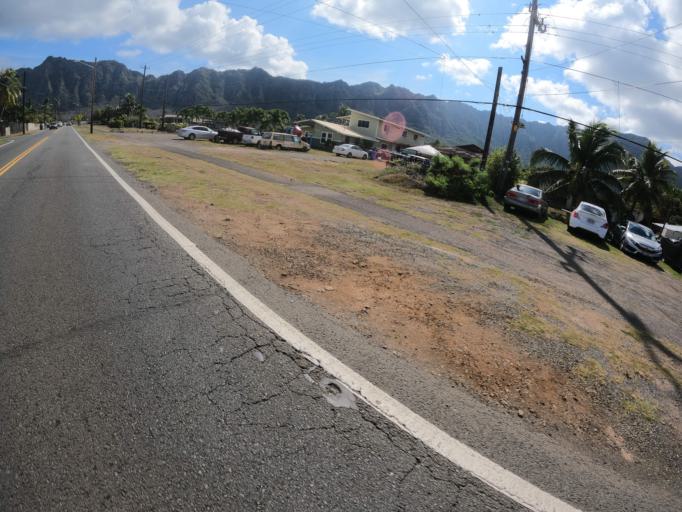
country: US
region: Hawaii
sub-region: Honolulu County
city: Waimanalo Beach
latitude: 21.3370
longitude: -157.7014
